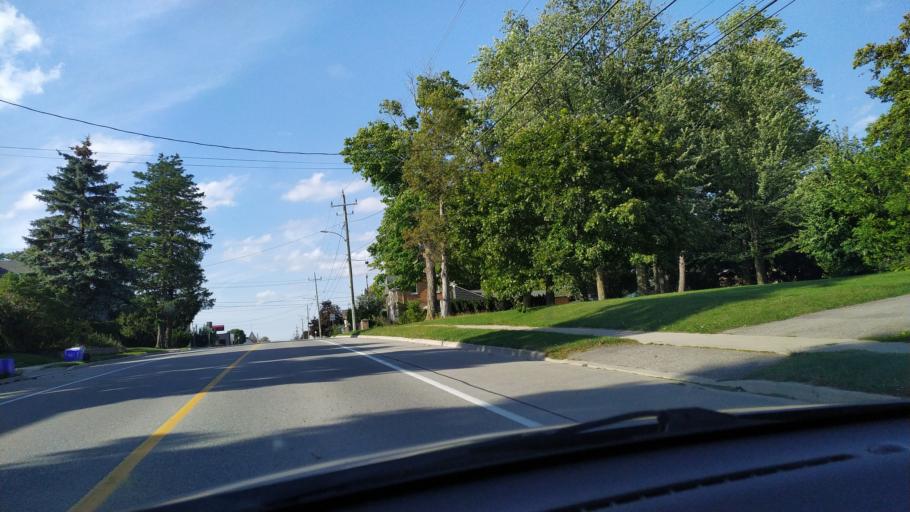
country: CA
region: Ontario
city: Ingersoll
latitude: 43.1527
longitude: -80.8995
